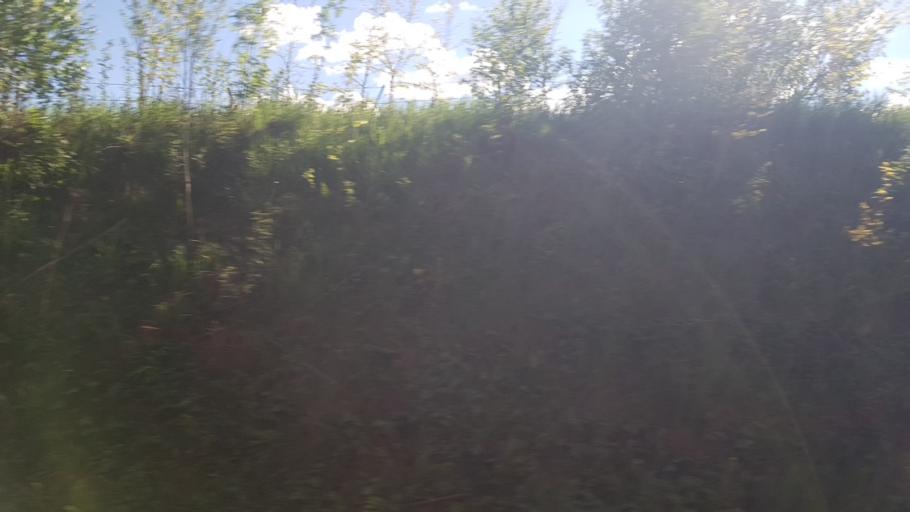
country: NO
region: Sor-Trondelag
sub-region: Midtre Gauldal
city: Storen
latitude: 62.9433
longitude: 10.1863
